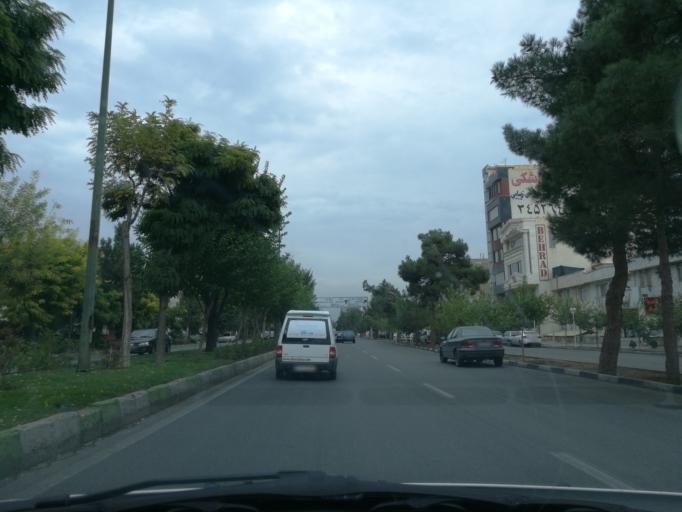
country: IR
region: Alborz
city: Karaj
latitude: 35.8587
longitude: 50.9457
